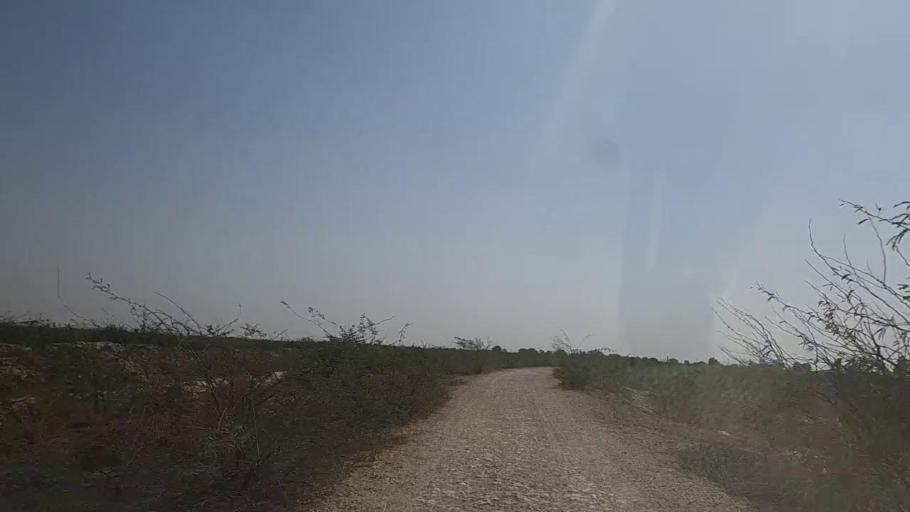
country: PK
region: Sindh
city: Naukot
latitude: 24.6340
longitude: 69.2726
